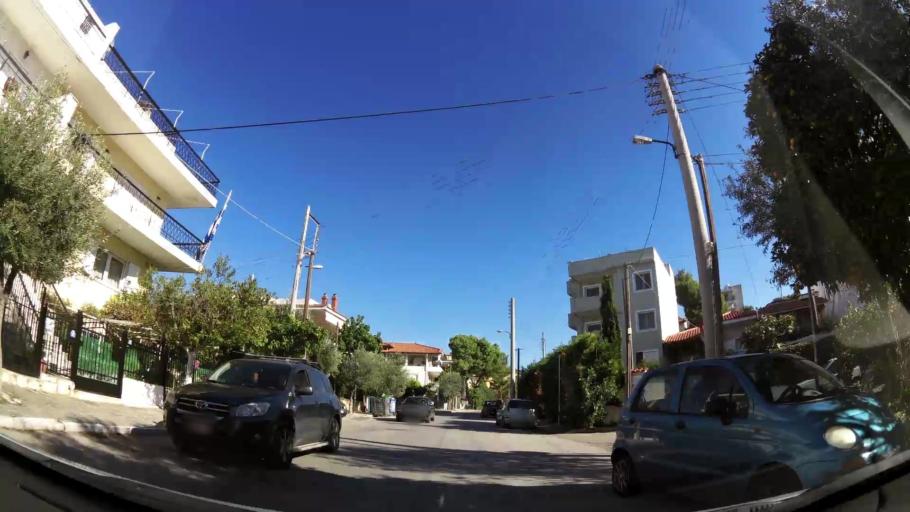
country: GR
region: Attica
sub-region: Nomarchia Athinas
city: Nea Erythraia
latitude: 38.0967
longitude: 23.8121
